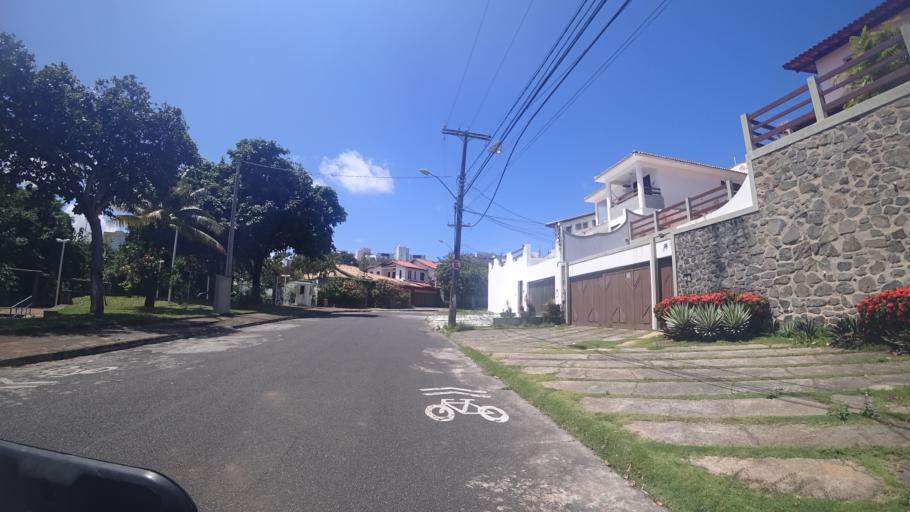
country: BR
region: Bahia
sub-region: Salvador
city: Salvador
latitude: -12.9924
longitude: -38.4687
